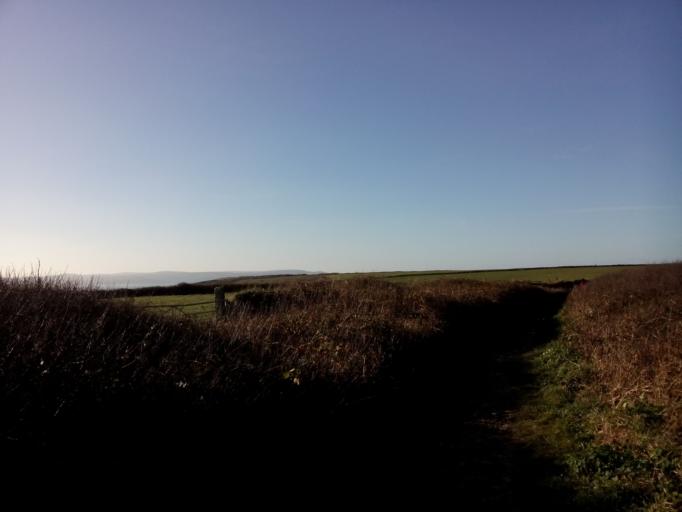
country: GB
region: England
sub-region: Cornwall
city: Hayle
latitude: 50.2363
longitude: -5.3720
